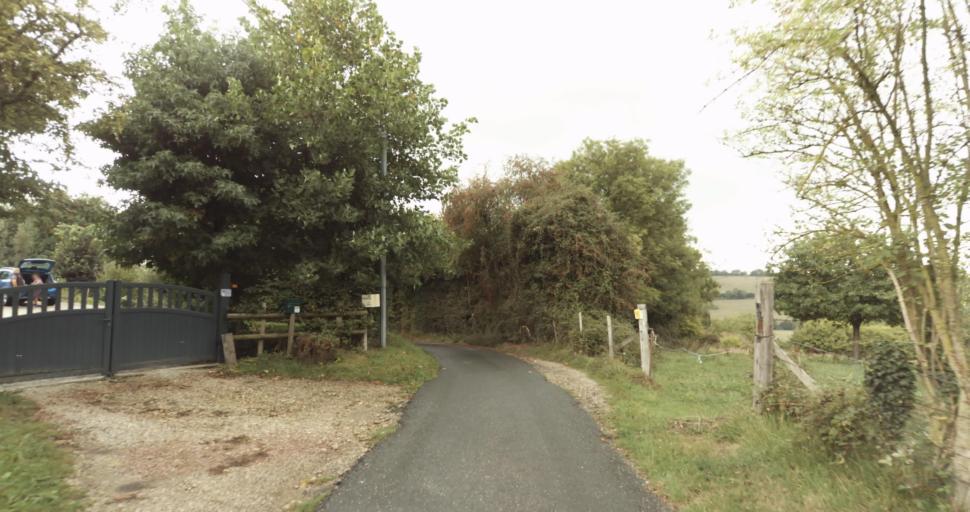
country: FR
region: Lower Normandy
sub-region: Departement de l'Orne
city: Vimoutiers
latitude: 48.9013
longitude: 0.1951
